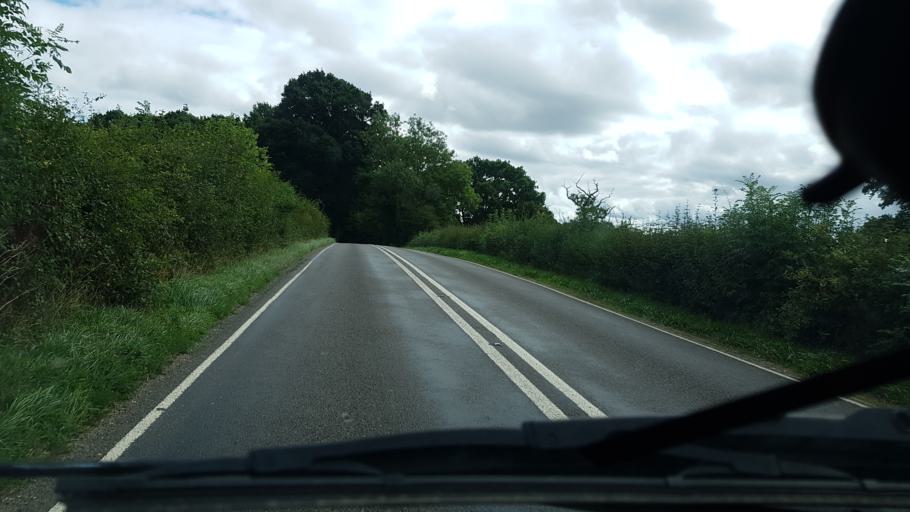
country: GB
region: England
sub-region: West Sussex
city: Rudgwick
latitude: 51.0863
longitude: -0.4232
